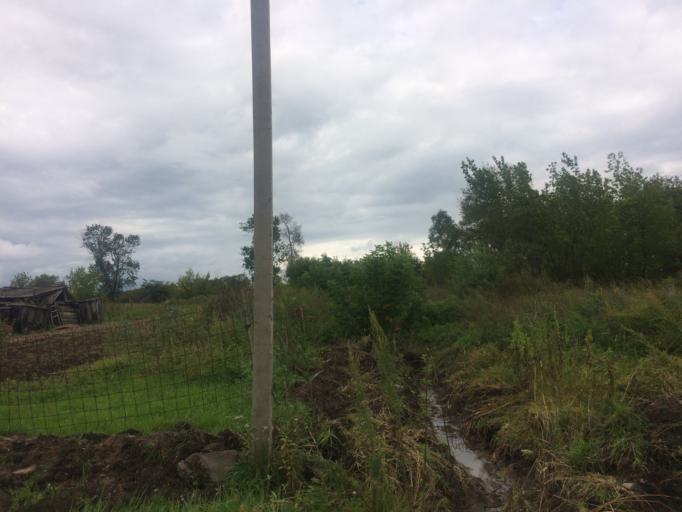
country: RU
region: Primorskiy
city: Lazo
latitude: 45.8317
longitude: 133.6142
